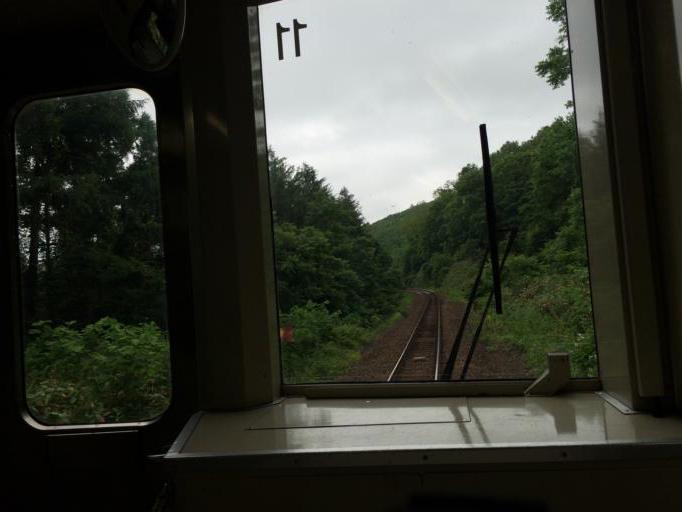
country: JP
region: Hokkaido
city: Otaru
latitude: 43.2095
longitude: 140.9360
